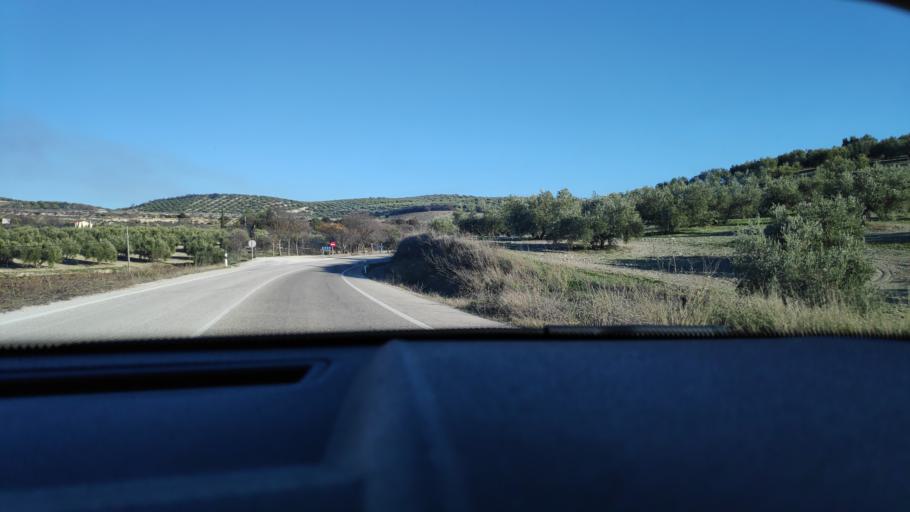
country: ES
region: Andalusia
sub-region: Province of Cordoba
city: Baena
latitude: 37.6005
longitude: -4.3088
